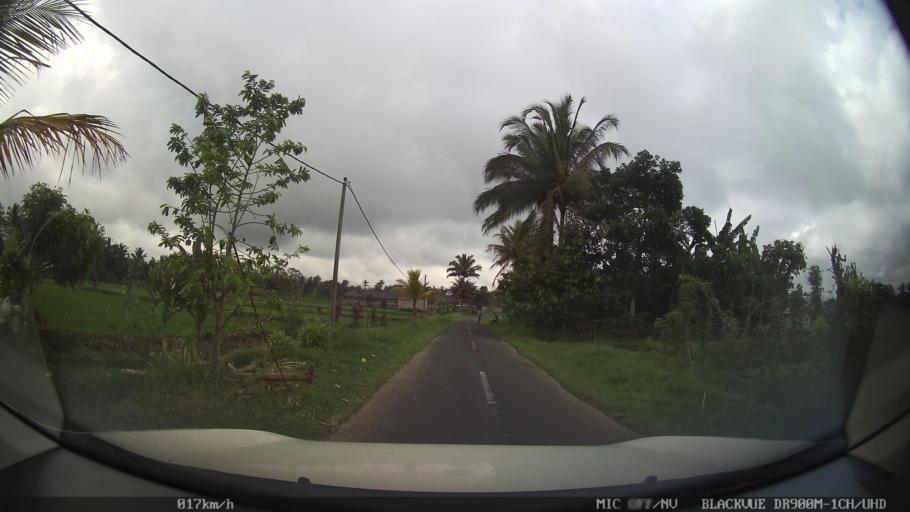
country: ID
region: Bali
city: Badung
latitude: -8.4202
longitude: 115.2270
